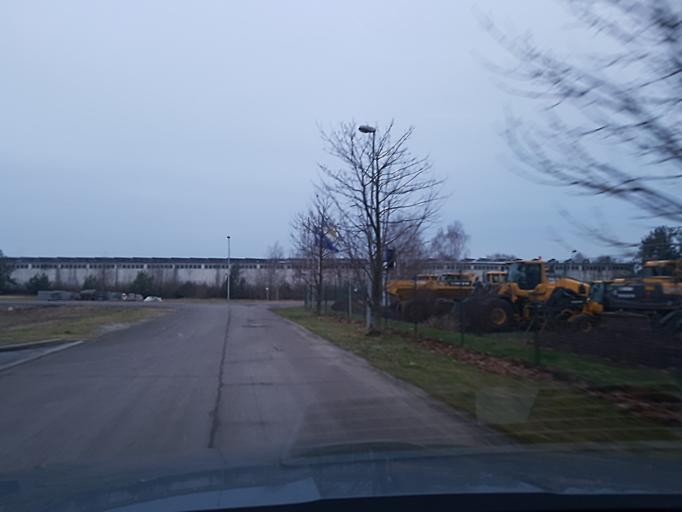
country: DE
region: Brandenburg
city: Doberlug-Kirchhain
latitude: 51.6289
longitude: 13.5844
